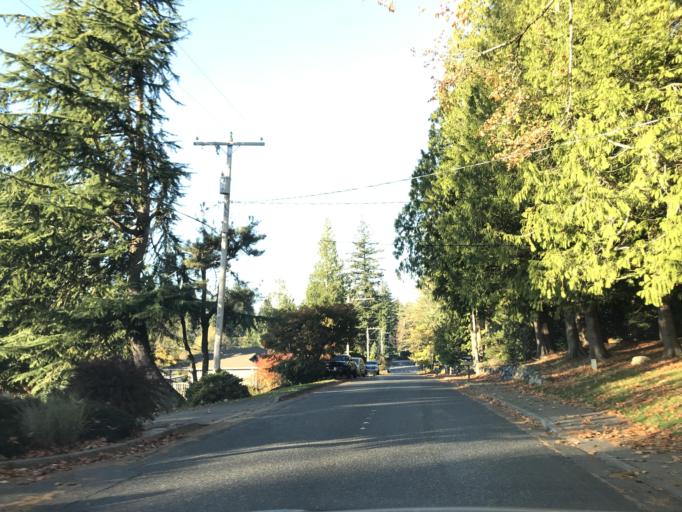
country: US
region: Washington
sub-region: Whatcom County
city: Geneva
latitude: 48.7465
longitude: -122.4263
